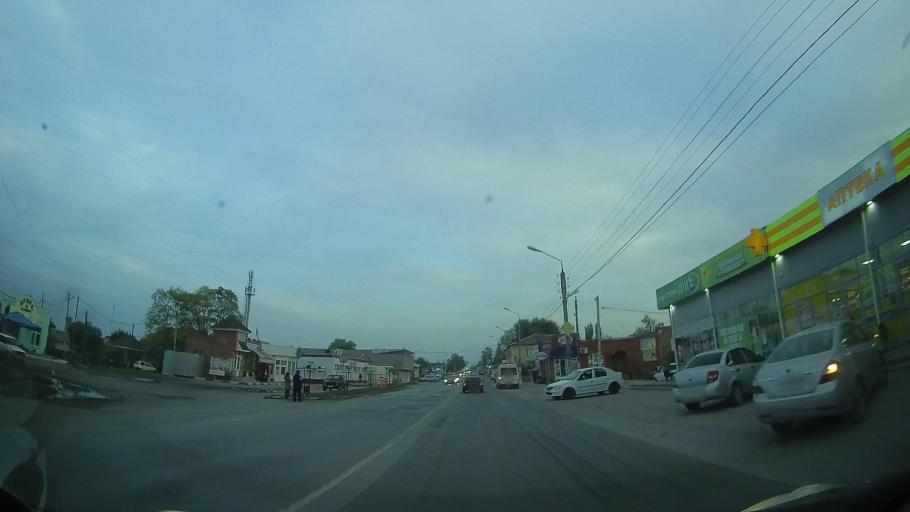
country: RU
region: Rostov
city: Kagal'nitskaya
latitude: 46.8827
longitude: 40.1482
